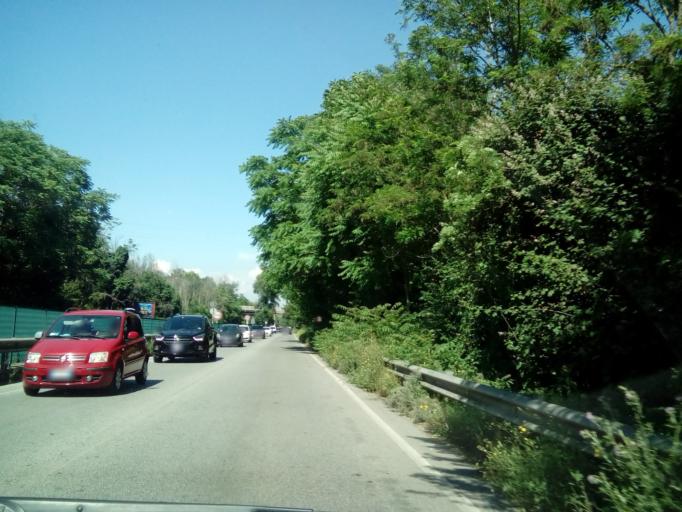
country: IT
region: Latium
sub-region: Citta metropolitana di Roma Capitale
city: Vitinia
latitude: 41.8342
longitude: 12.4555
